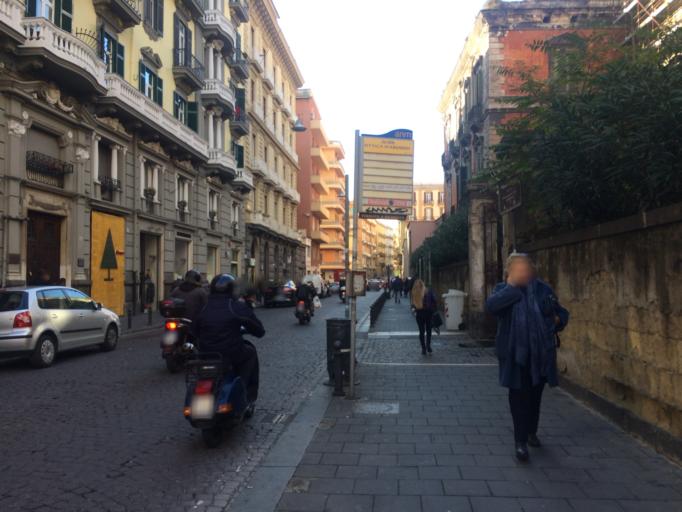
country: IT
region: Campania
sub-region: Provincia di Napoli
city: Napoli
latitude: 40.8366
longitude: 14.2381
